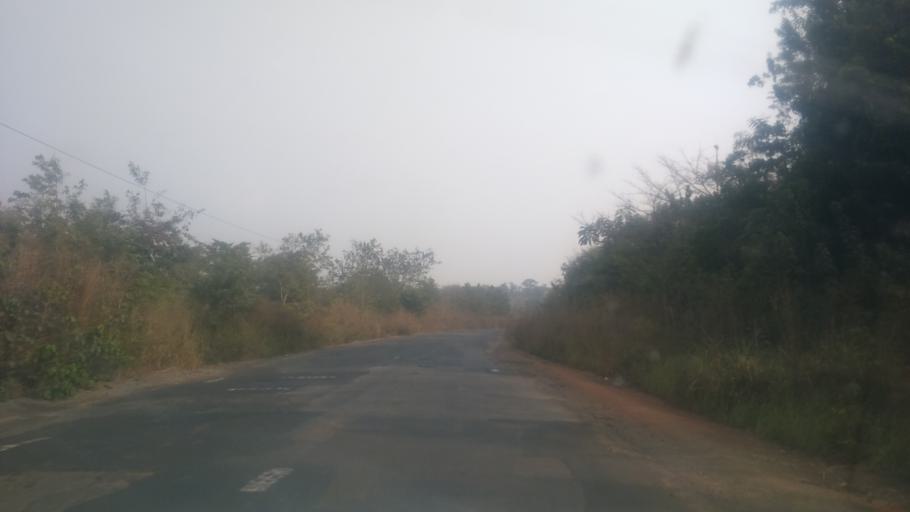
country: CM
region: West
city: Tonga
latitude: 4.9924
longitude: 10.7027
